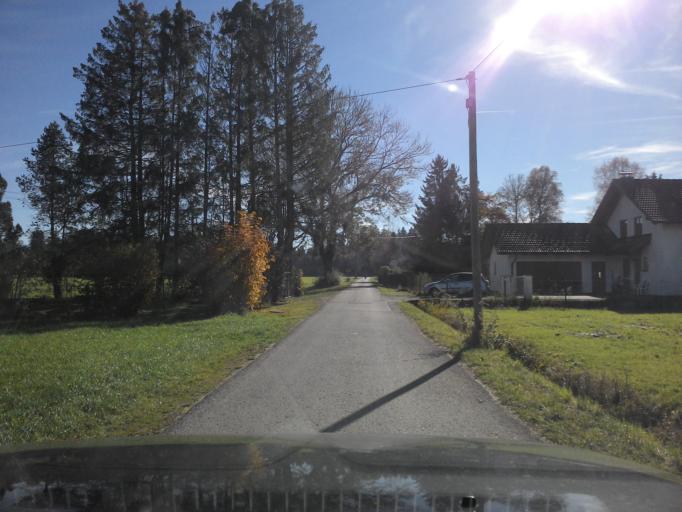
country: DE
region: Bavaria
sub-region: Upper Bavaria
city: Seeshaupt
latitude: 47.8179
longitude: 11.3258
